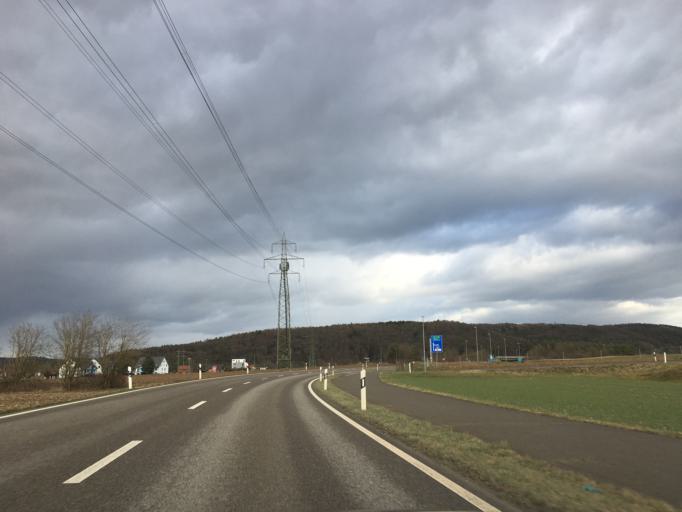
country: CH
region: Zurich
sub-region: Bezirk Buelach
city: Glattfelden
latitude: 47.5658
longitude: 8.4674
